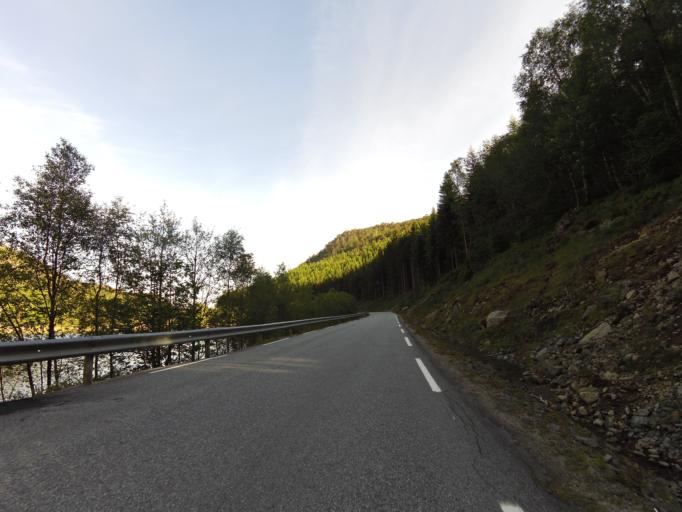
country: NO
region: Vest-Agder
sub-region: Flekkefjord
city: Flekkefjord
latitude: 58.2838
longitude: 6.6182
